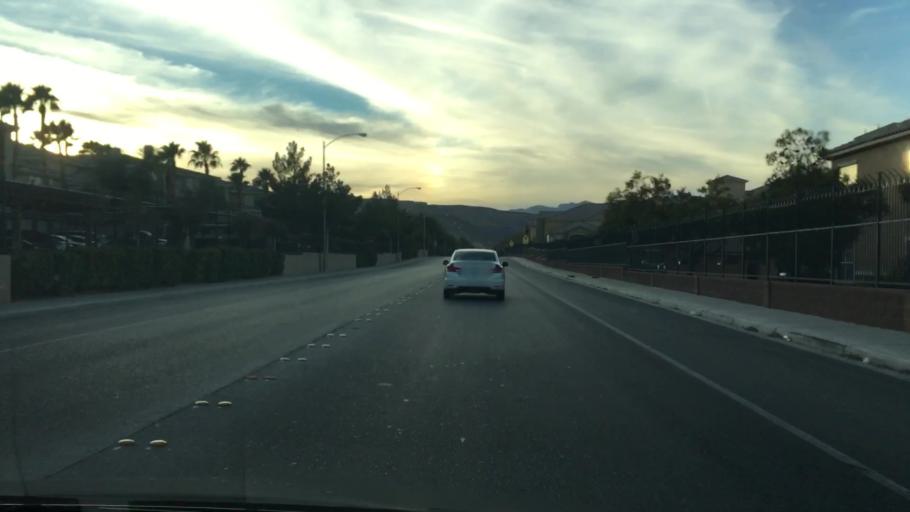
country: US
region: Nevada
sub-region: Clark County
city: Enterprise
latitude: 36.0593
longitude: -115.2814
